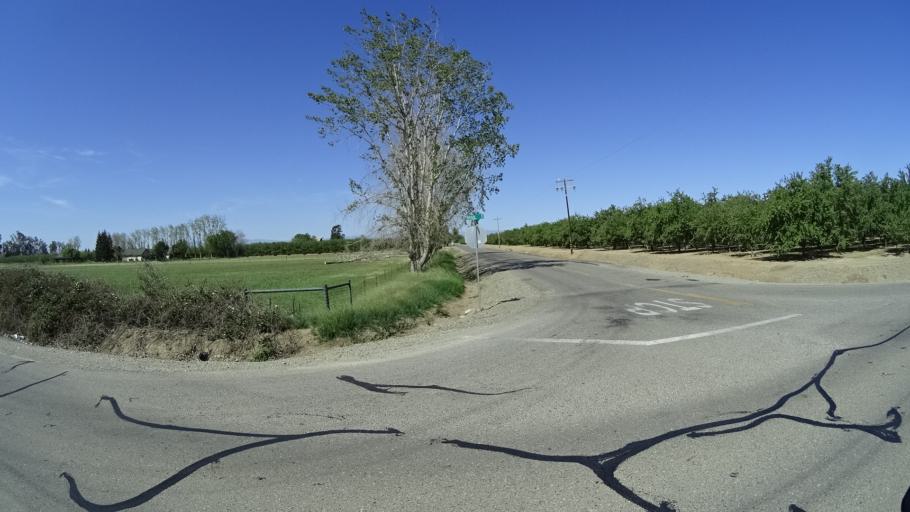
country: US
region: California
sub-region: Glenn County
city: Hamilton City
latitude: 39.7247
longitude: -122.1043
